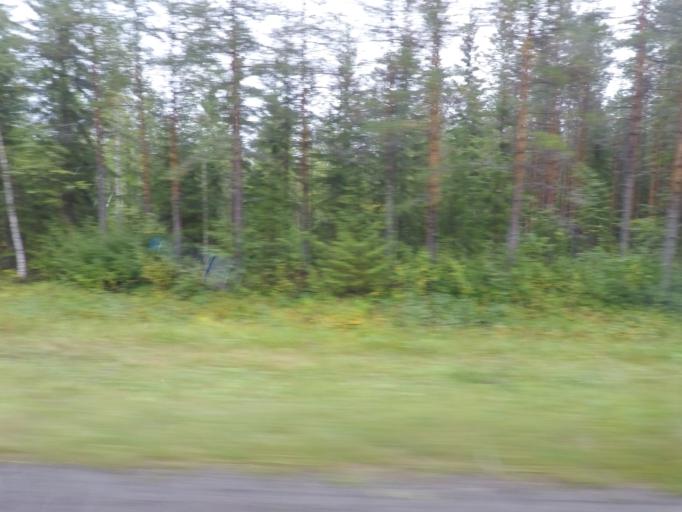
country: FI
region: Southern Savonia
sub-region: Pieksaemaeki
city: Joroinen
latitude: 62.1288
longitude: 27.8392
